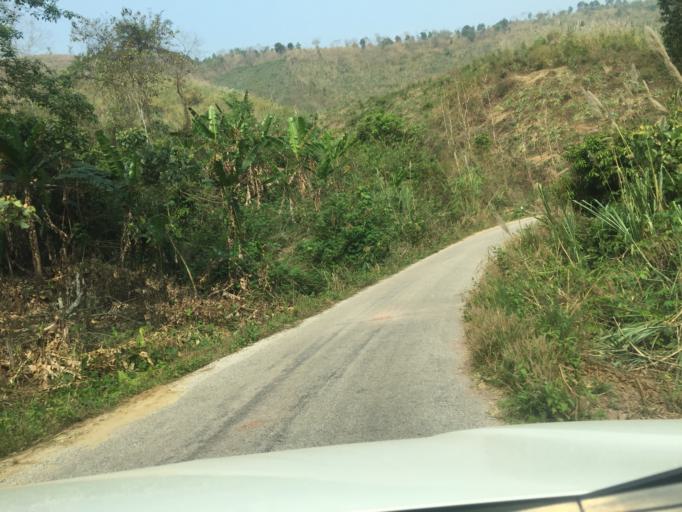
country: LA
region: Xiagnabouli
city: Sainyabuli
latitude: 19.3001
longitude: 101.4828
